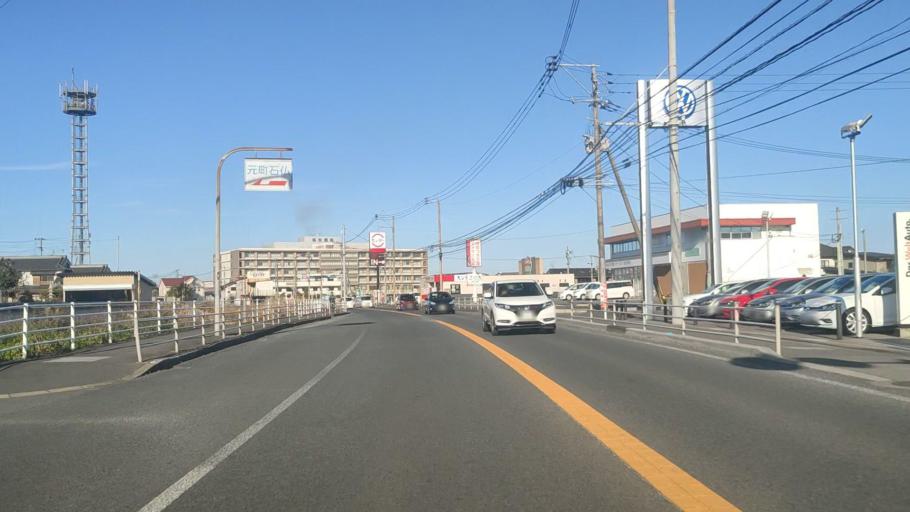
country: JP
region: Oita
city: Oita
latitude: 33.2215
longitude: 131.6176
